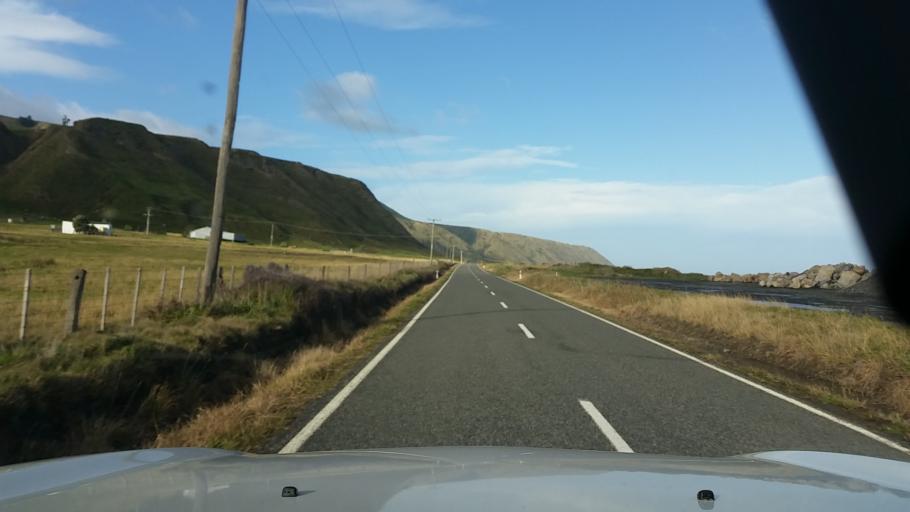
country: NZ
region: Wellington
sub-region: South Wairarapa District
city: Waipawa
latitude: -41.4830
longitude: 175.2087
